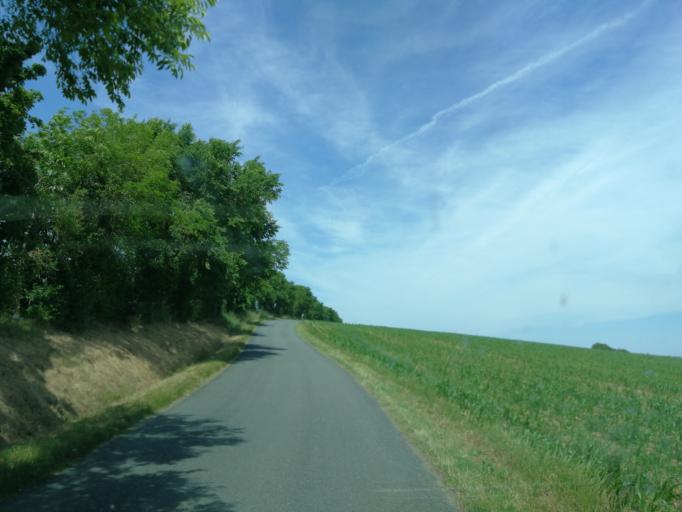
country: FR
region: Pays de la Loire
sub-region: Departement de la Vendee
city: Le Langon
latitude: 46.4289
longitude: -0.8905
